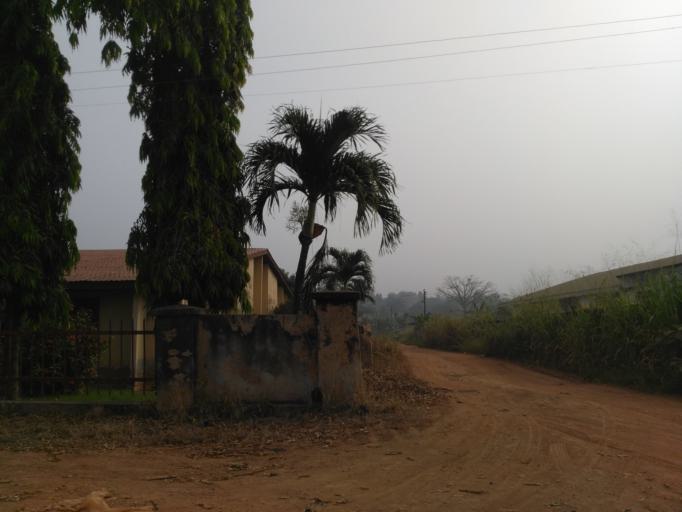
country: GH
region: Ashanti
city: Kumasi
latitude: 6.6528
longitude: -1.6247
